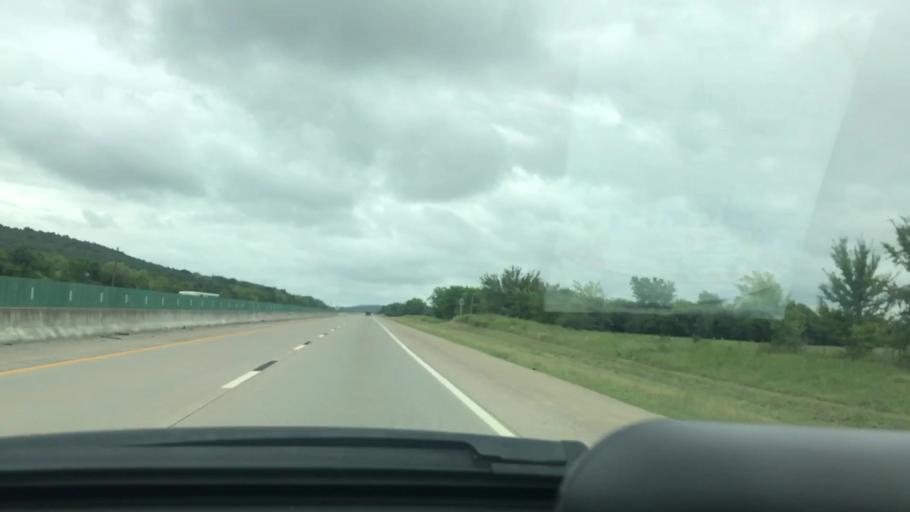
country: US
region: Oklahoma
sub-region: Pittsburg County
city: Krebs
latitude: 35.0672
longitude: -95.7055
